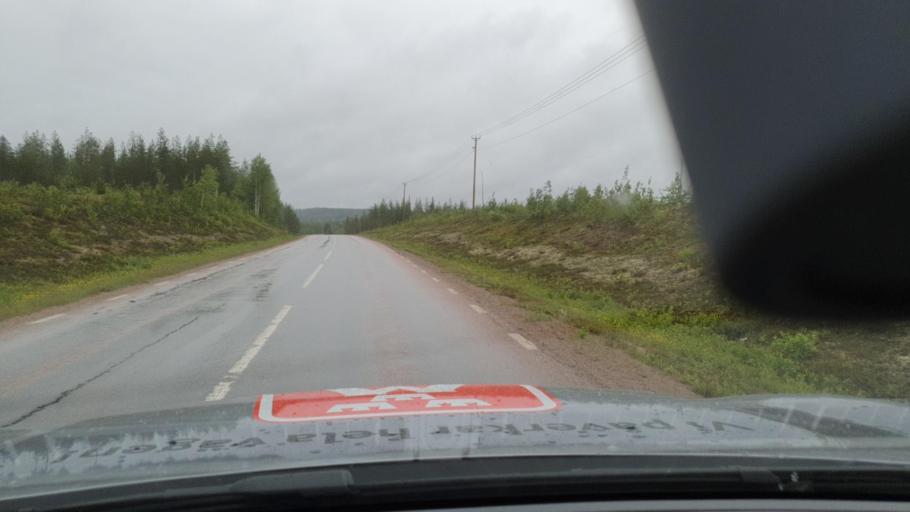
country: SE
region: Norrbotten
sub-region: Overkalix Kommun
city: OEverkalix
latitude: 66.3803
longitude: 22.9137
